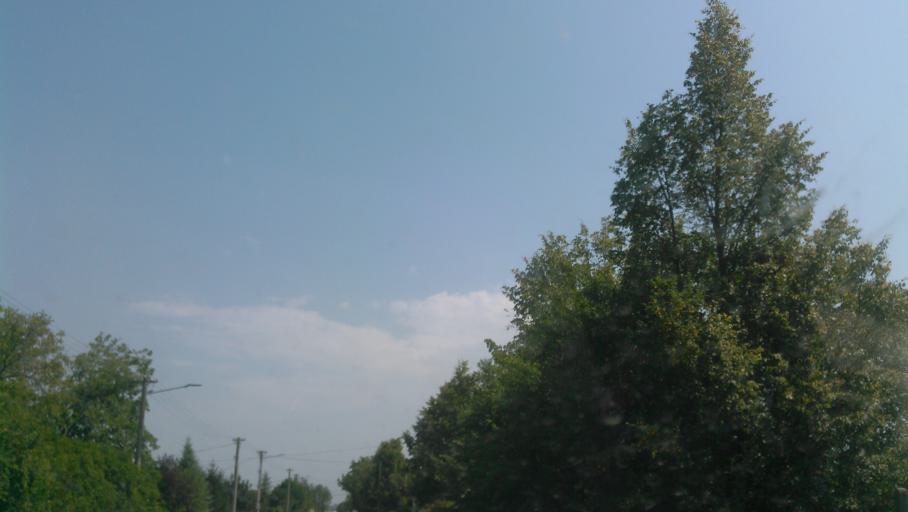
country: SK
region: Trnavsky
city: Dunajska Streda
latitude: 48.0360
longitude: 17.5309
